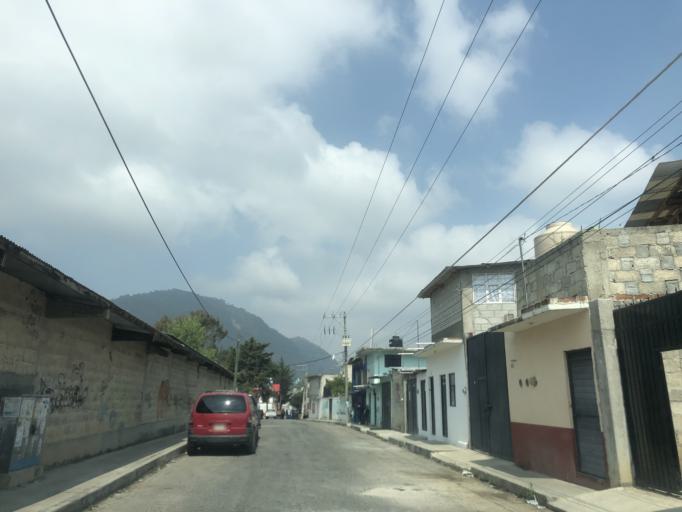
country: MX
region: Chiapas
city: San Cristobal de las Casas
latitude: 16.7163
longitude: -92.6425
